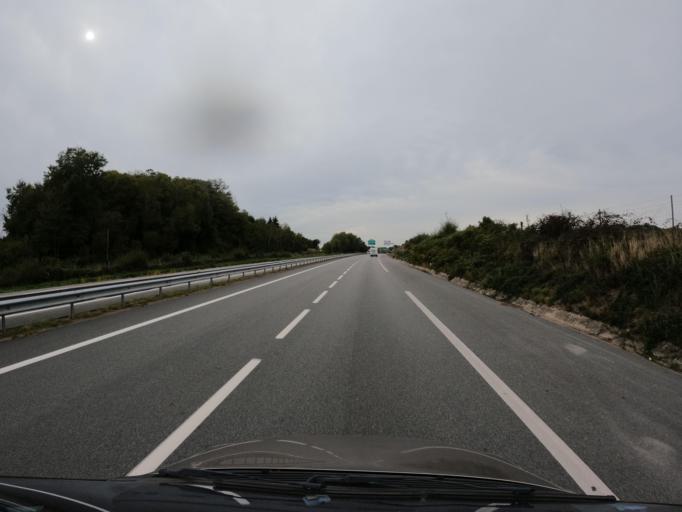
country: FR
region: Limousin
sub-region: Departement de la Creuse
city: Le Grand-Bourg
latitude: 46.2213
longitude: 1.5887
